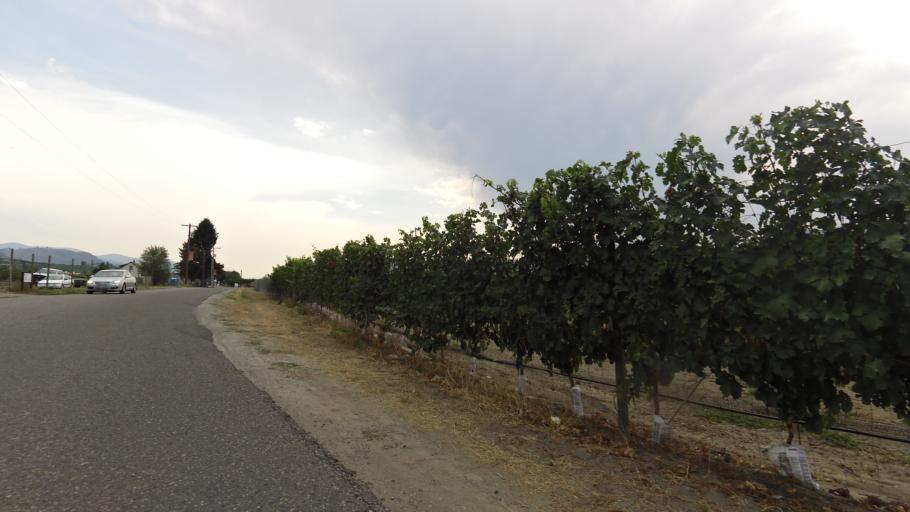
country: CA
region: British Columbia
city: Osoyoos
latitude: 49.0357
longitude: -119.4367
